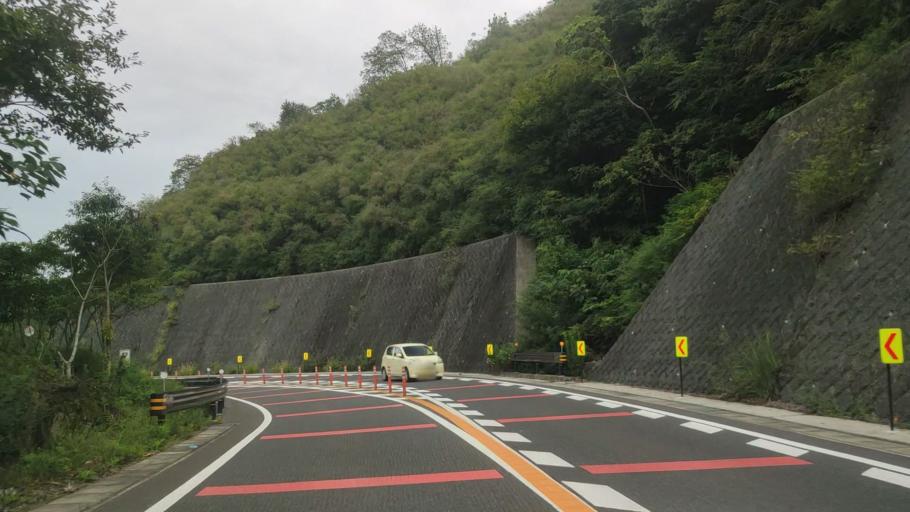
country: JP
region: Wakayama
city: Hashimoto
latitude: 34.3985
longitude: 135.5969
